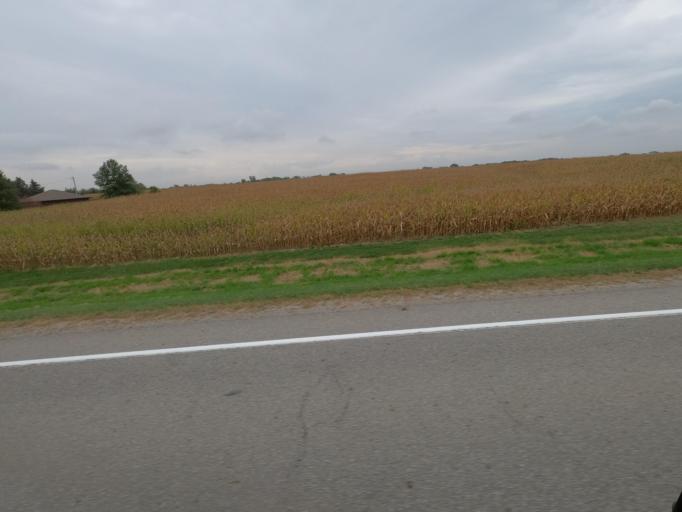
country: US
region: Iowa
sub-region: Van Buren County
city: Keosauqua
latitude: 40.8135
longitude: -91.8885
